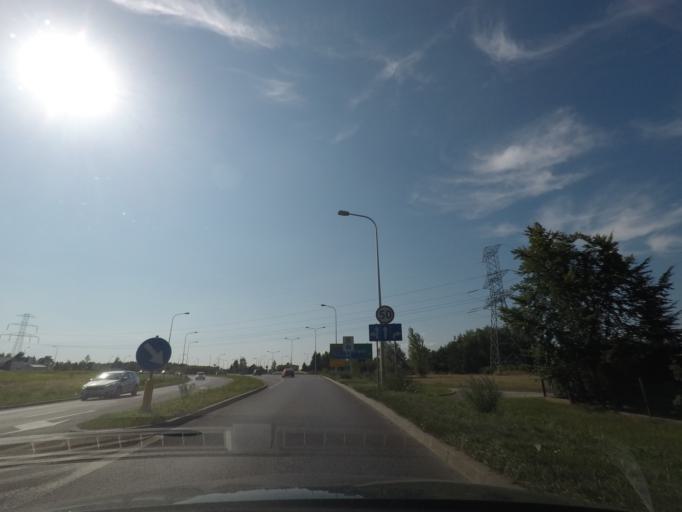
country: PL
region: Silesian Voivodeship
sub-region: Zory
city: Zory
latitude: 50.0613
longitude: 18.6653
